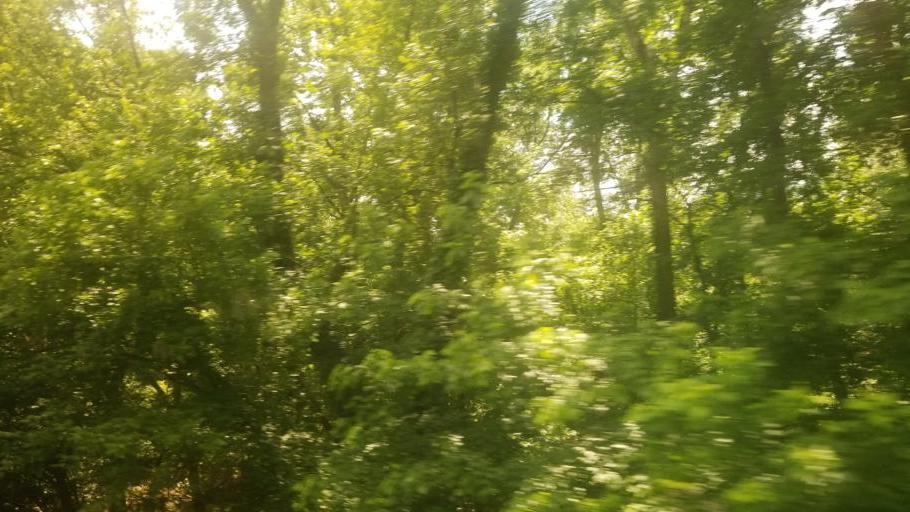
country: US
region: Maryland
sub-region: Frederick County
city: Point of Rocks
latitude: 39.2701
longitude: -77.5284
